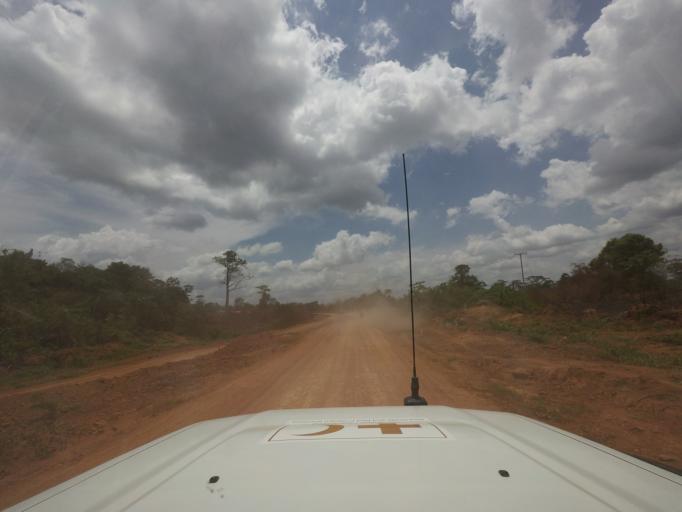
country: LR
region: Nimba
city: Sanniquellie
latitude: 7.2639
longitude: -8.8480
